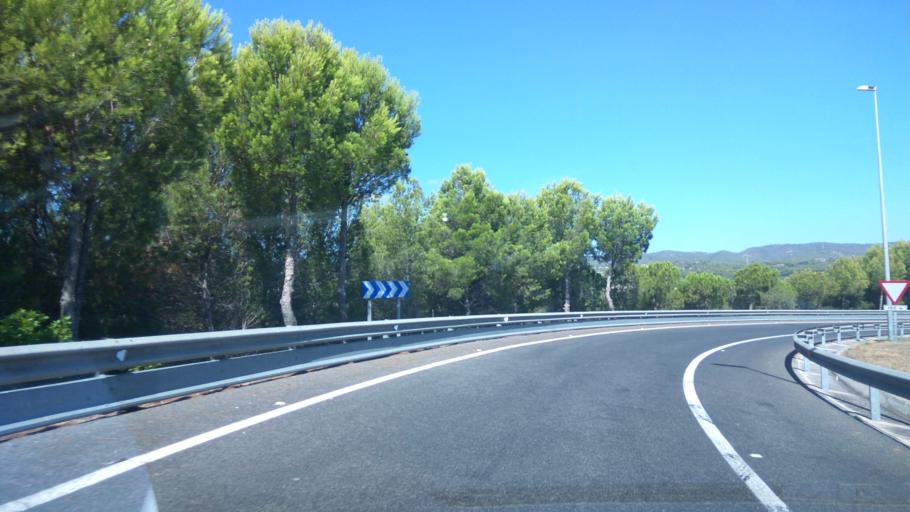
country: ES
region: Catalonia
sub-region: Provincia de Tarragona
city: El Vendrell
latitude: 41.1946
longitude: 1.5370
